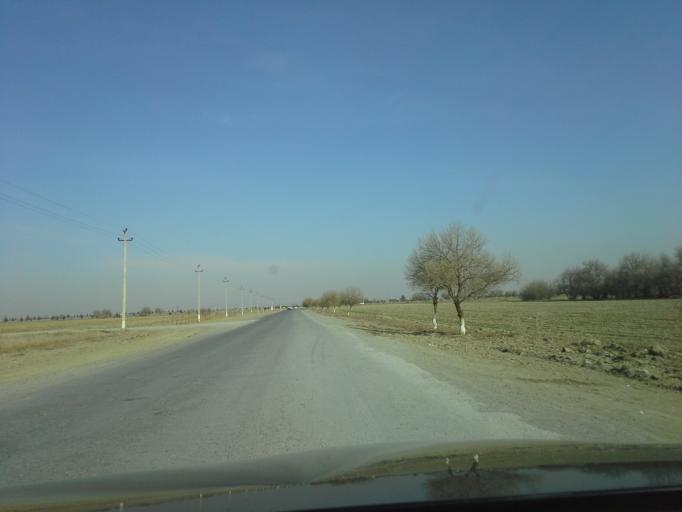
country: TM
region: Ahal
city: Abadan
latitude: 38.1316
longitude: 58.0038
